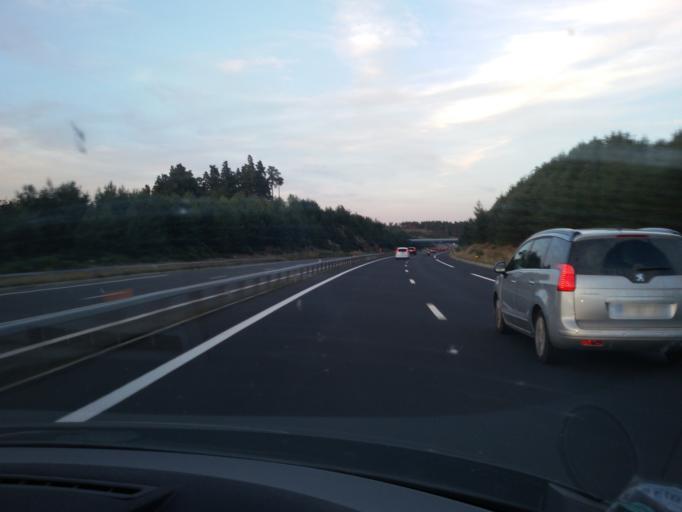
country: FR
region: Languedoc-Roussillon
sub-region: Departement de la Lozere
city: Aumont-Aubrac
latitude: 44.6842
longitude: 3.2651
